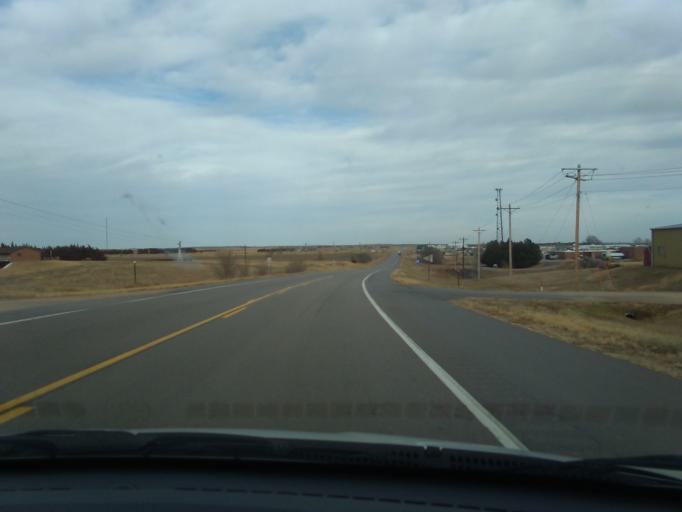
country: US
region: Nebraska
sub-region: Dundy County
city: Benkelman
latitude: 40.0555
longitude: -101.5410
